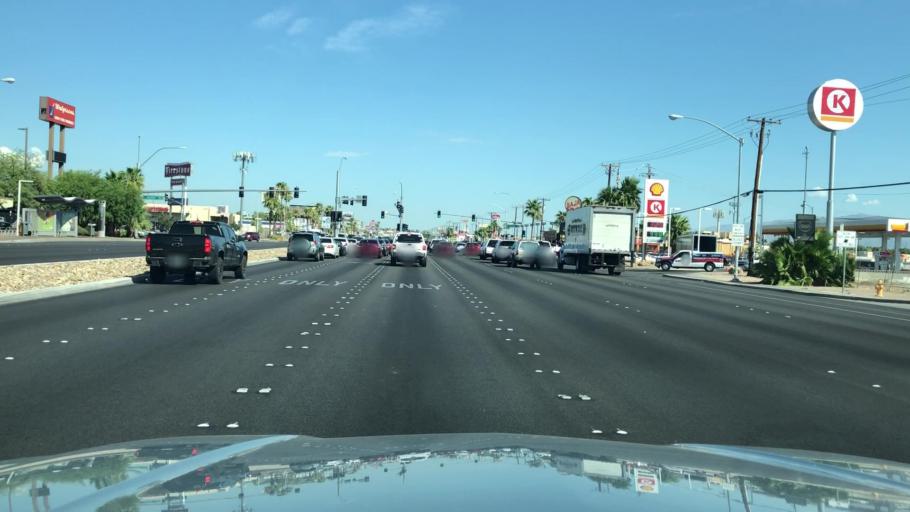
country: US
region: Nevada
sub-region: Clark County
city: Winchester
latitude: 36.1449
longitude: -115.1005
